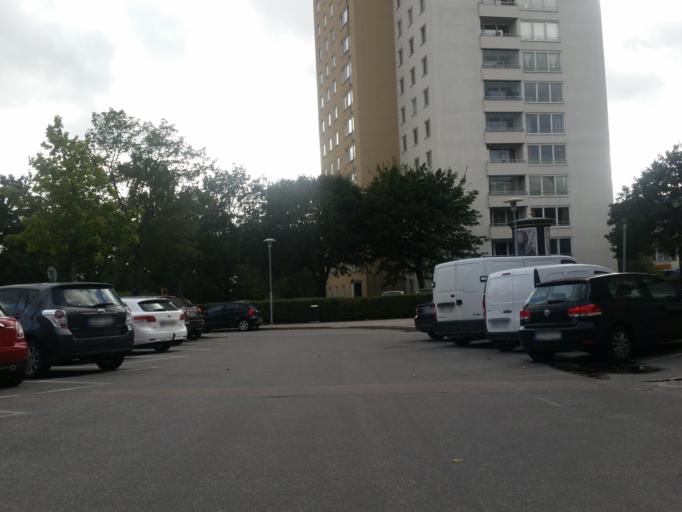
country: SE
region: Stockholm
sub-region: Stockholms Kommun
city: Arsta
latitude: 59.2422
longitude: 18.0921
